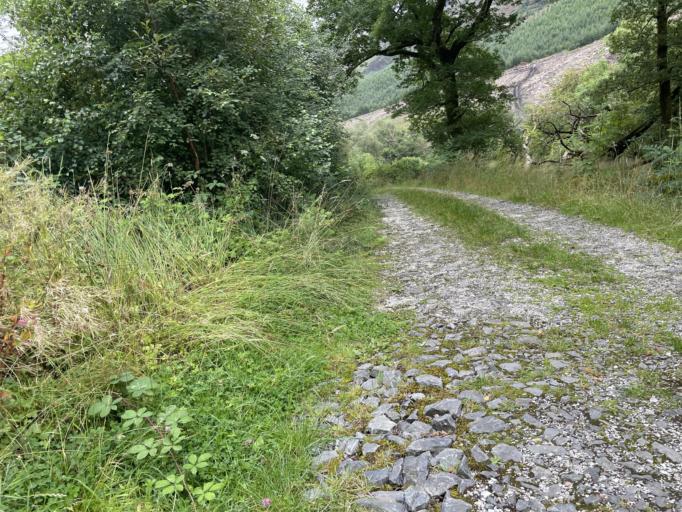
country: GB
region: Scotland
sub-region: Dumfries and Galloway
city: Newton Stewart
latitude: 55.0899
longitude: -4.4593
